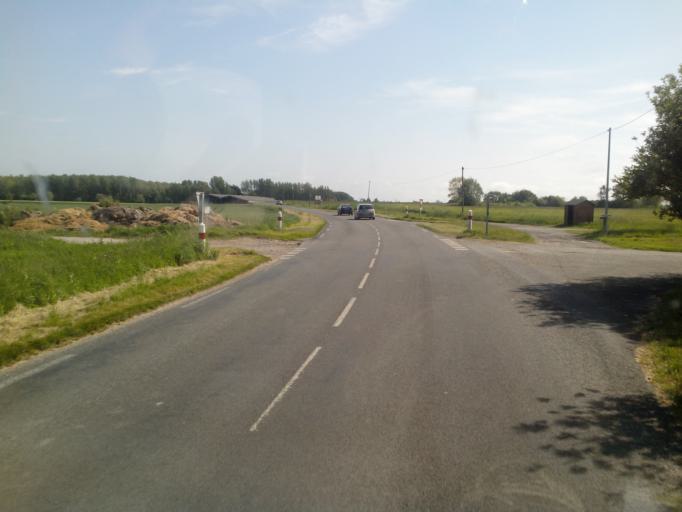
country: FR
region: Picardie
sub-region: Departement de la Somme
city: Quend
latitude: 50.3357
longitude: 1.6438
